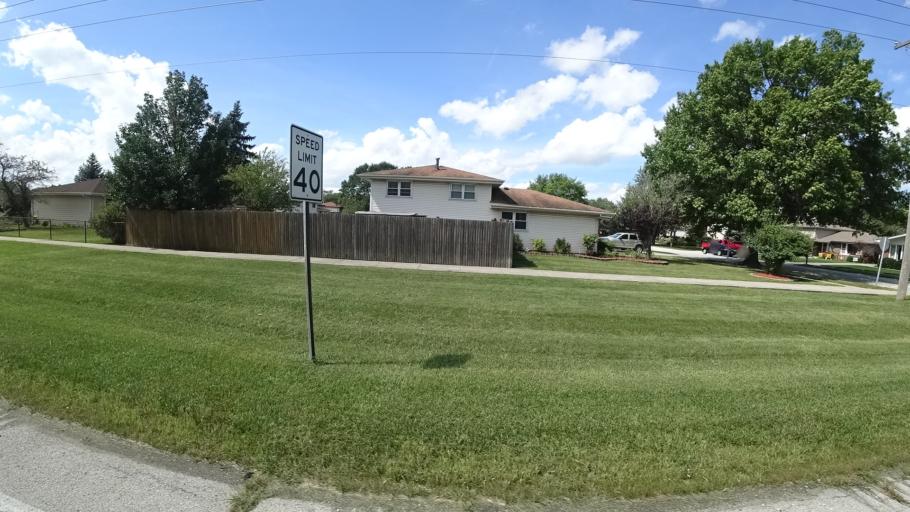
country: US
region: Illinois
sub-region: Cook County
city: Tinley Park
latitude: 41.5622
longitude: -87.7742
